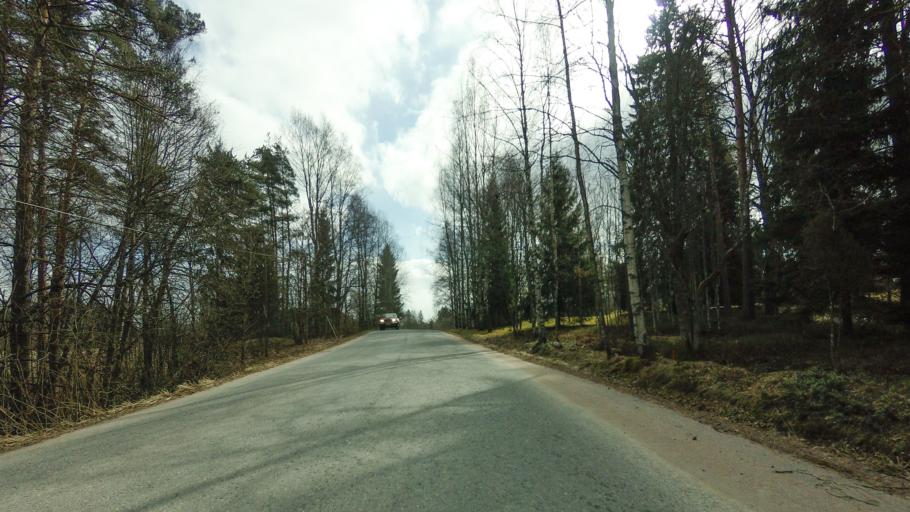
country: FI
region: Varsinais-Suomi
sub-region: Salo
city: Suomusjaervi
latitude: 60.3451
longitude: 23.6789
